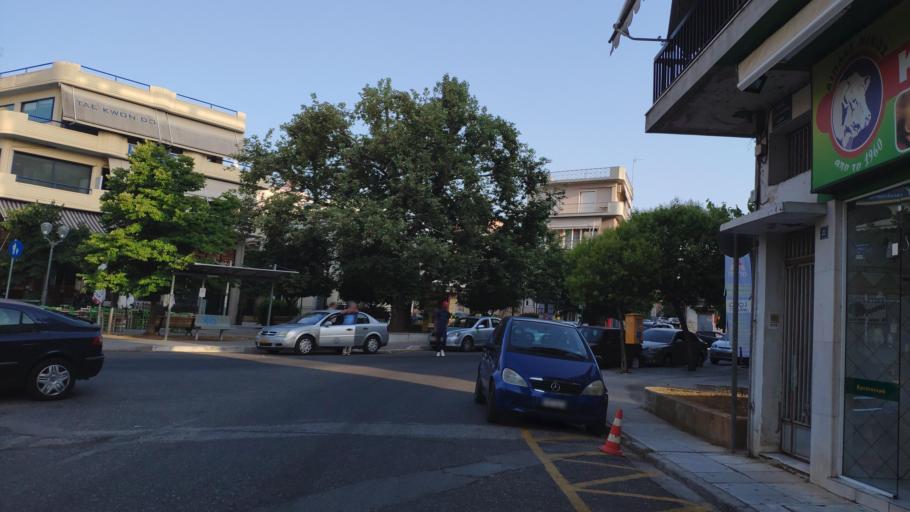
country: GR
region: West Greece
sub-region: Nomos Aitolias kai Akarnanias
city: Agrinio
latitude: 38.6208
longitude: 21.4116
